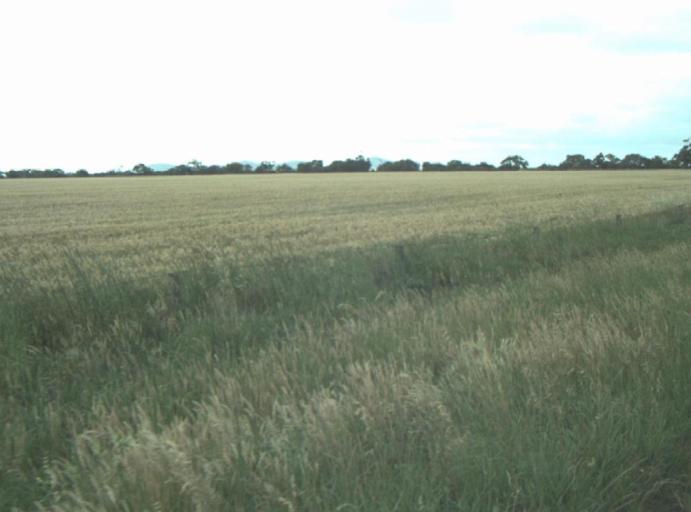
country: AU
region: Victoria
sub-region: Wyndham
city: Wyndham Vale
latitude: -37.8395
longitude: 144.3556
